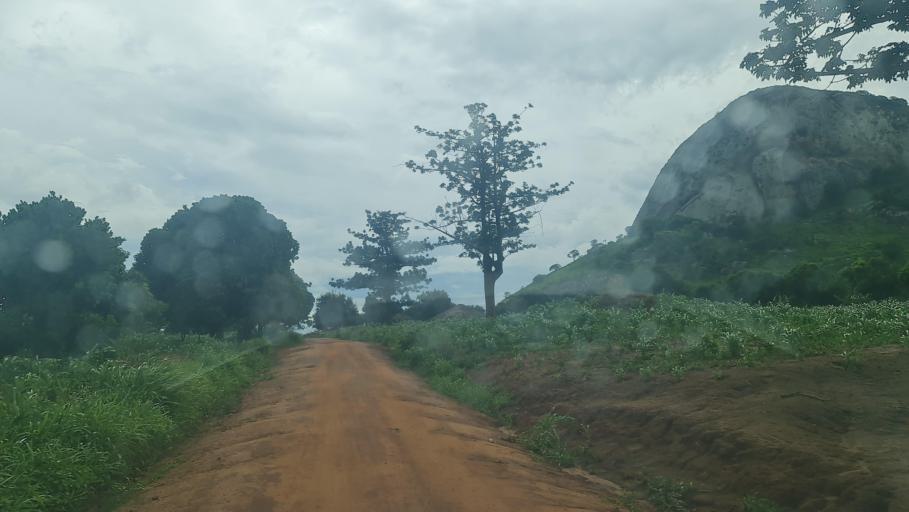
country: MW
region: Southern Region
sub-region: Nsanje District
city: Nsanje
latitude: -17.3964
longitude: 35.5826
